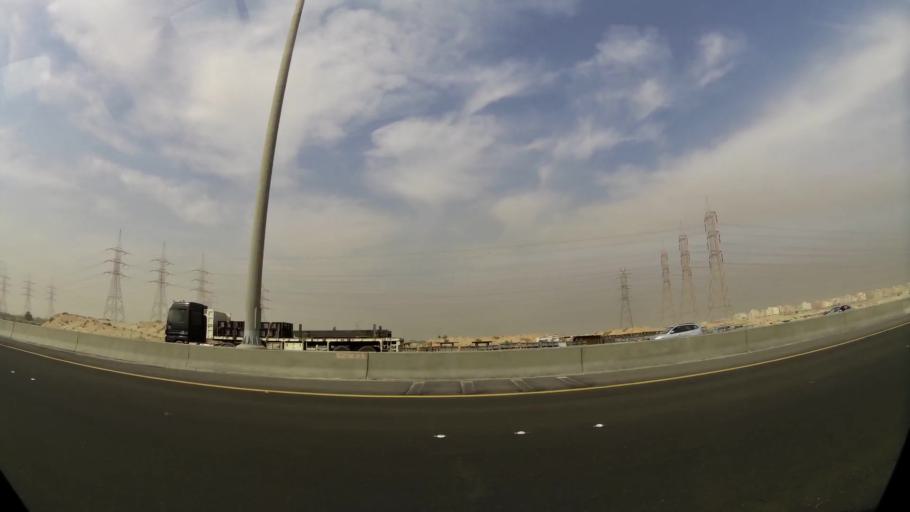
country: KW
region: Muhafazat al Jahra'
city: Al Jahra'
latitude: 29.3185
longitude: 47.7853
